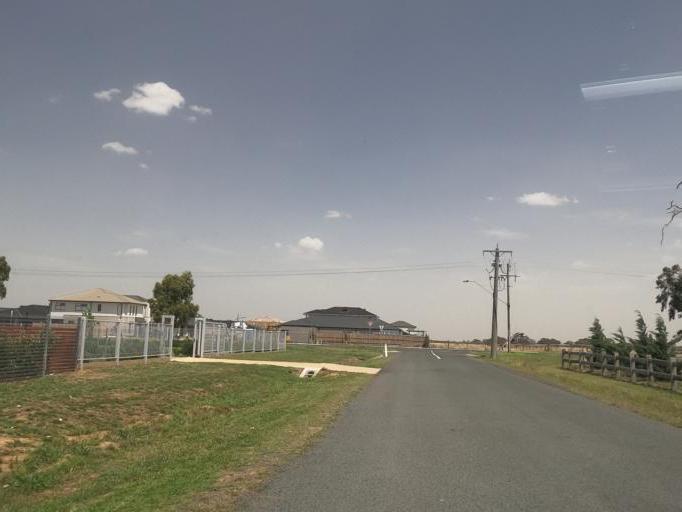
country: AU
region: Victoria
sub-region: Hume
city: Craigieburn
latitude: -37.5629
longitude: 144.8910
